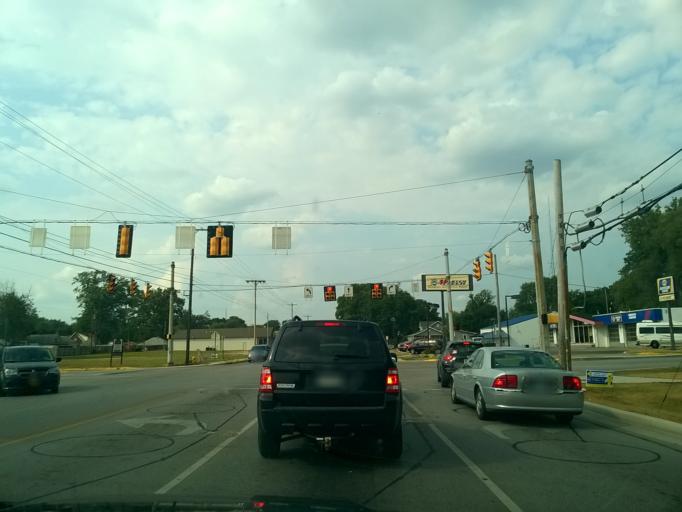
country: US
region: Indiana
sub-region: Vigo County
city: Terre Haute
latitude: 39.4266
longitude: -87.4068
